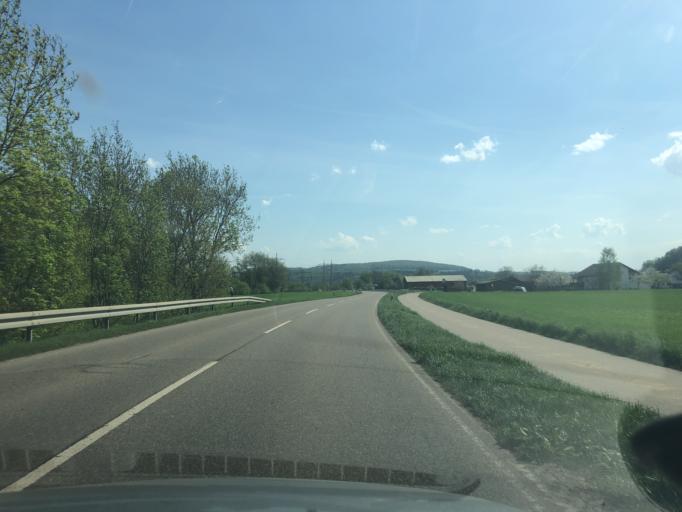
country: CH
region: Aargau
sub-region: Bezirk Zurzach
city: Koblenz
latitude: 47.6344
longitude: 8.2515
